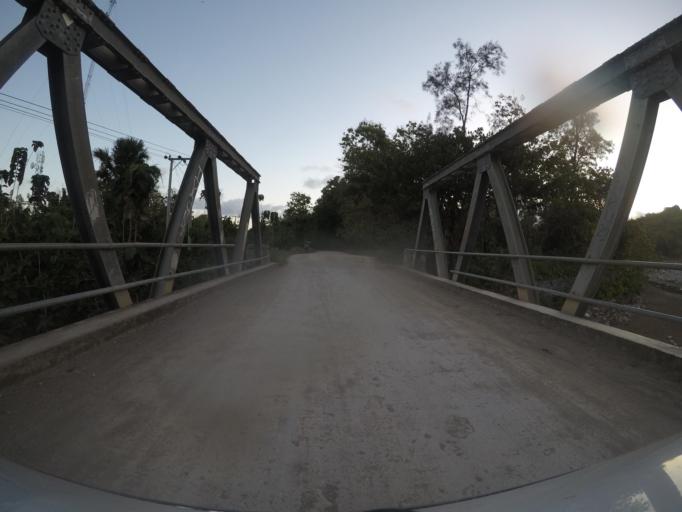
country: TL
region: Viqueque
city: Viqueque
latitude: -8.7678
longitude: 126.6440
